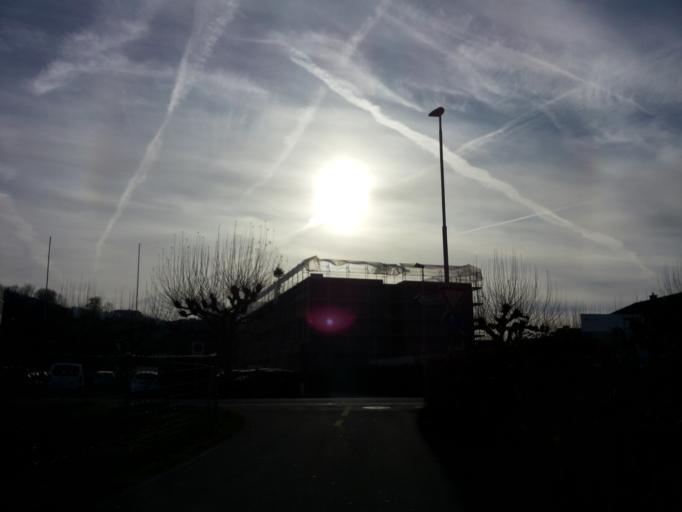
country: CH
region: Zug
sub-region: Zug
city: Zug
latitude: 47.1760
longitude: 8.5230
